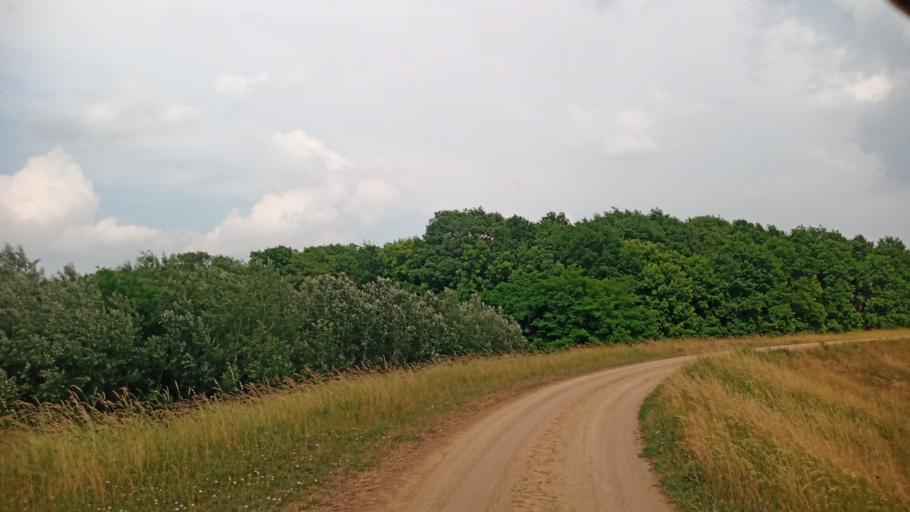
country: HU
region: Bekes
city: Doboz
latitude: 46.7073
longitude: 21.2824
